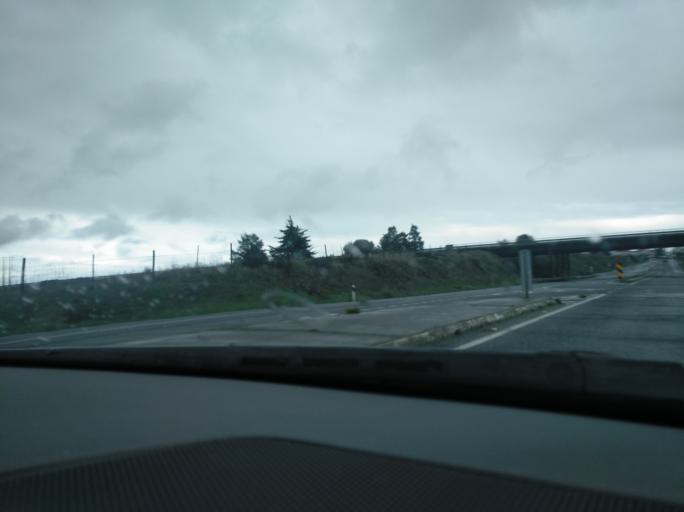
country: PT
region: Beja
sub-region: Castro Verde
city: Castro Verde
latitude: 37.7096
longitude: -8.0850
